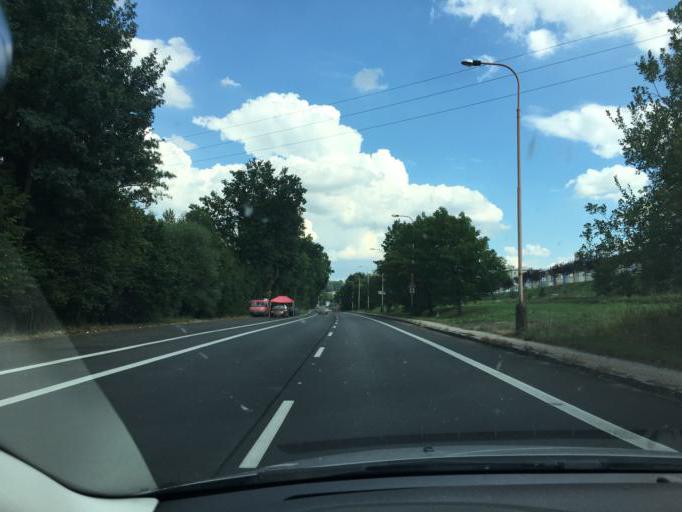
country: CZ
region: Liberecky
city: Jilemnice
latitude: 50.6260
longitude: 15.4943
